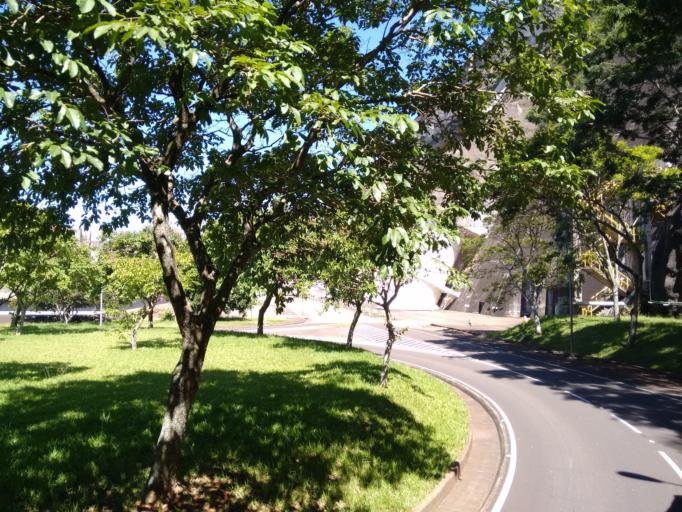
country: PY
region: Alto Parana
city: Ciudad del Este
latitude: -25.4090
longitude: -54.5840
